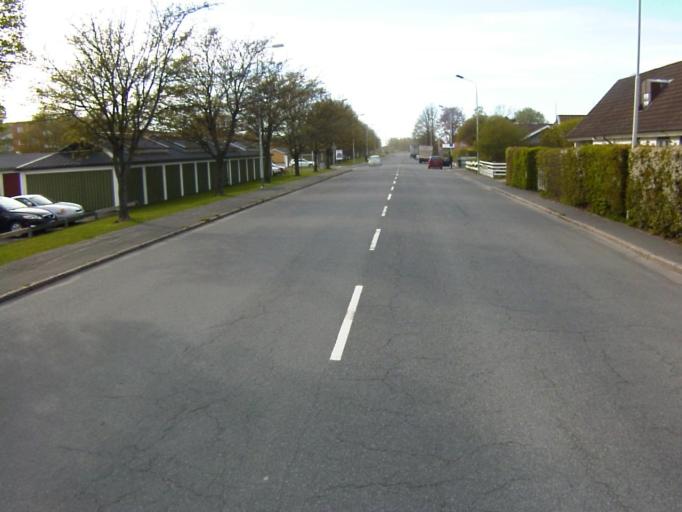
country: SE
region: Skane
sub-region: Kristianstads Kommun
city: Kristianstad
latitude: 56.0604
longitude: 14.1618
